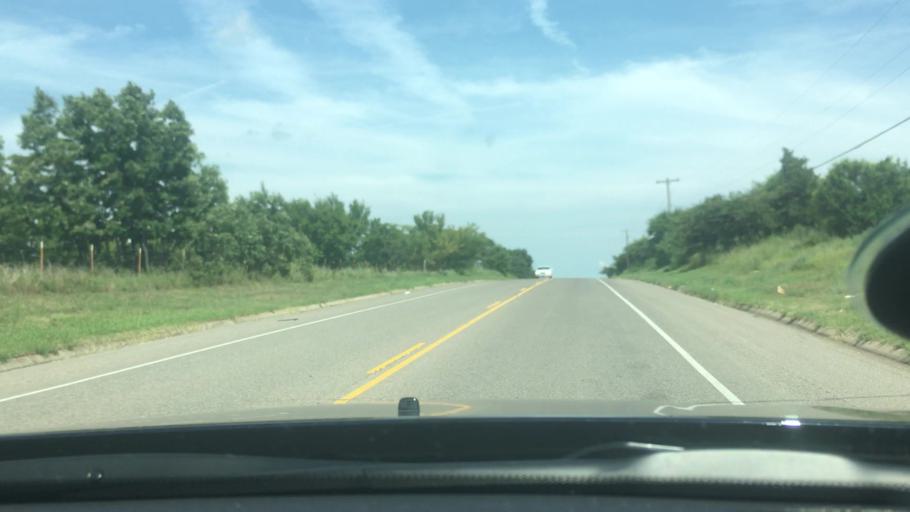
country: US
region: Oklahoma
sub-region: Pottawatomie County
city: Shawnee
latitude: 35.3331
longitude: -96.8384
